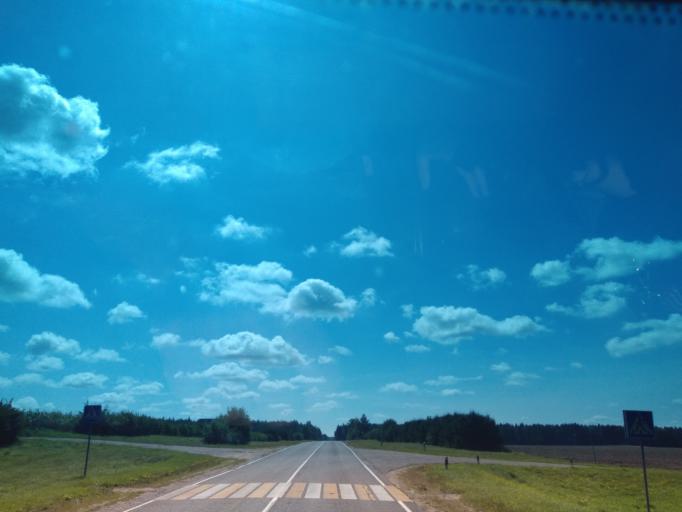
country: BY
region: Minsk
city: Uzda
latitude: 53.3378
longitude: 27.2291
